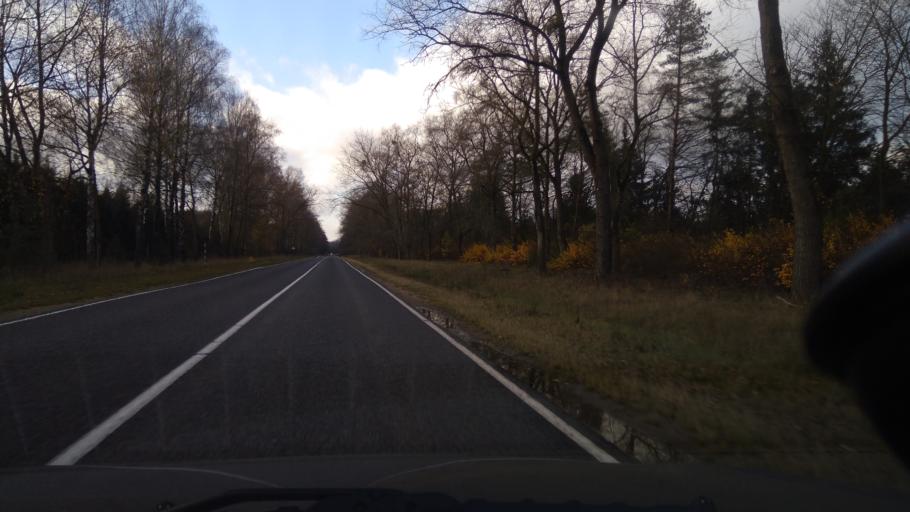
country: BY
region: Minsk
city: Slutsk
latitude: 53.2315
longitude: 27.6565
